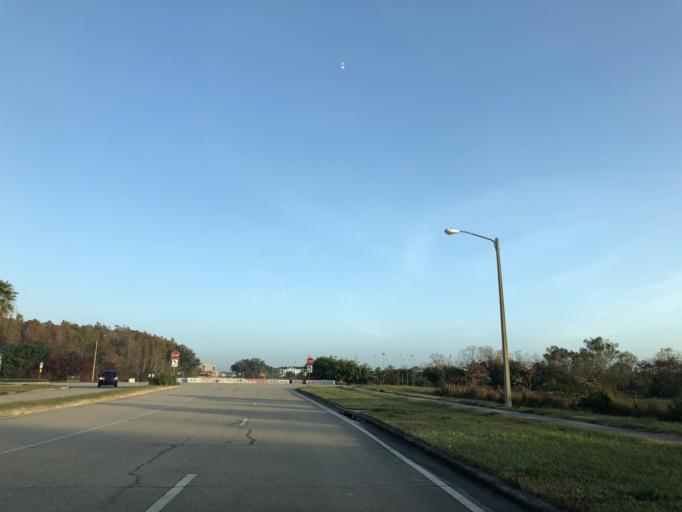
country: US
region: Florida
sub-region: Osceola County
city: Kissimmee
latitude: 28.3301
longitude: -81.4244
